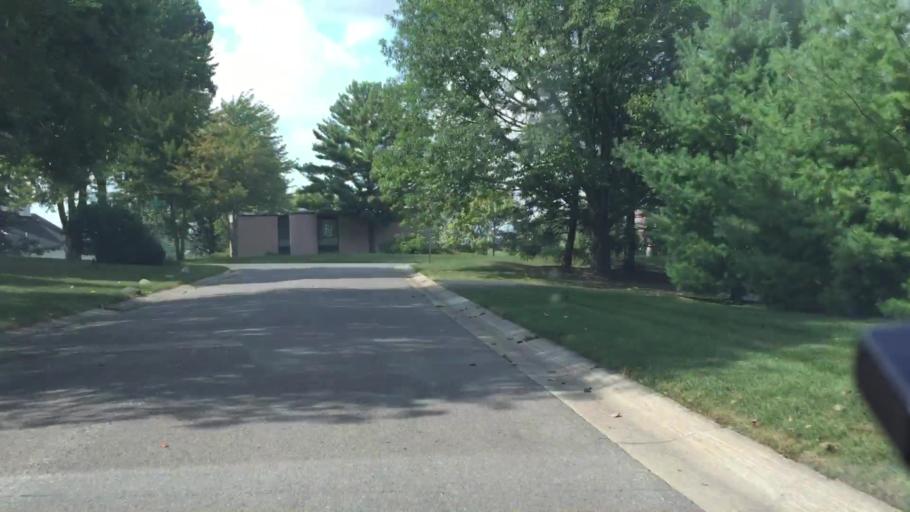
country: US
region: Michigan
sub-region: Oakland County
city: Sylvan Lake
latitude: 42.5738
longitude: -83.3104
